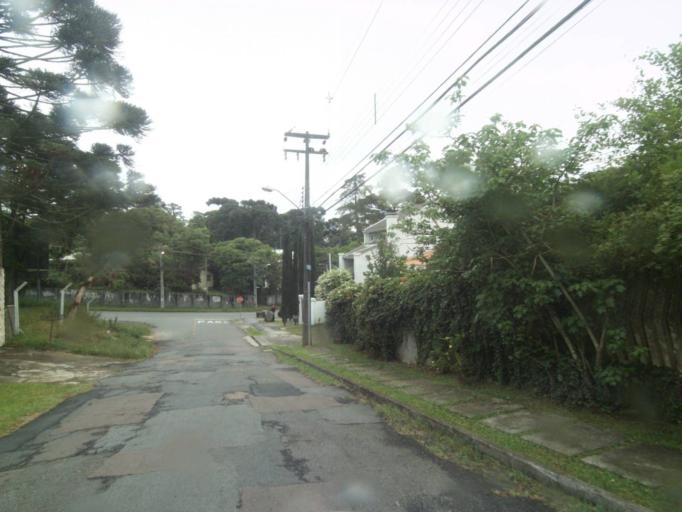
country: BR
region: Parana
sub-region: Curitiba
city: Curitiba
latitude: -25.4223
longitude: -49.3230
